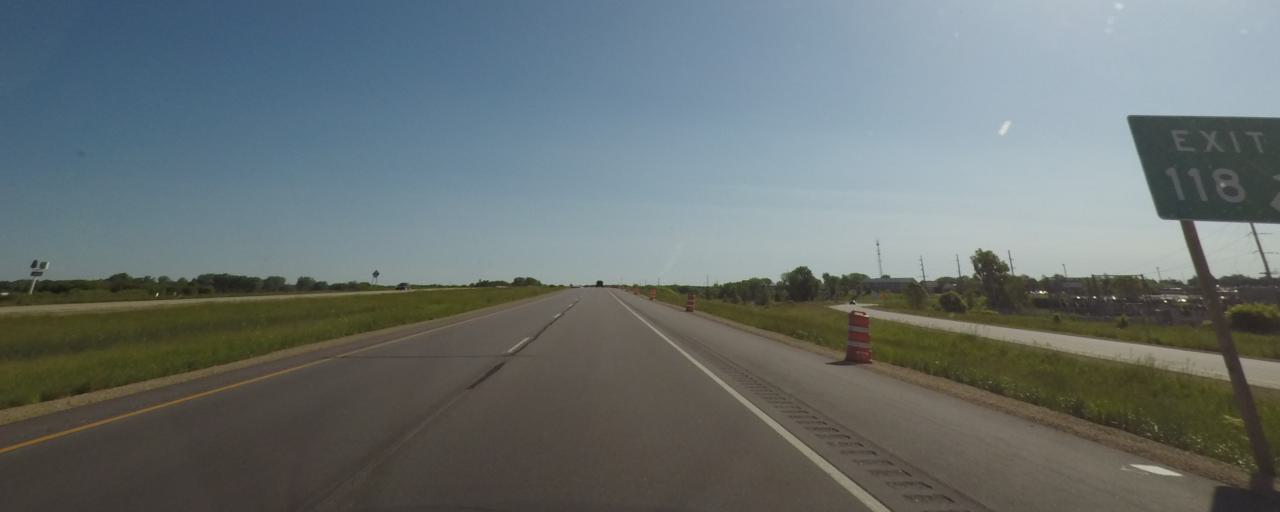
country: US
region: Wisconsin
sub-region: Columbia County
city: Columbus
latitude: 43.3450
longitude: -89.0374
